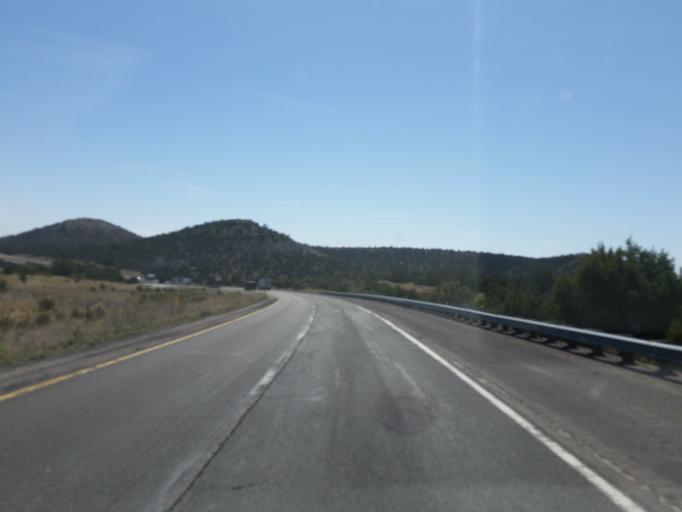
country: US
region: Arizona
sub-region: Mohave County
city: Peach Springs
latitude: 35.2922
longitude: -113.0368
